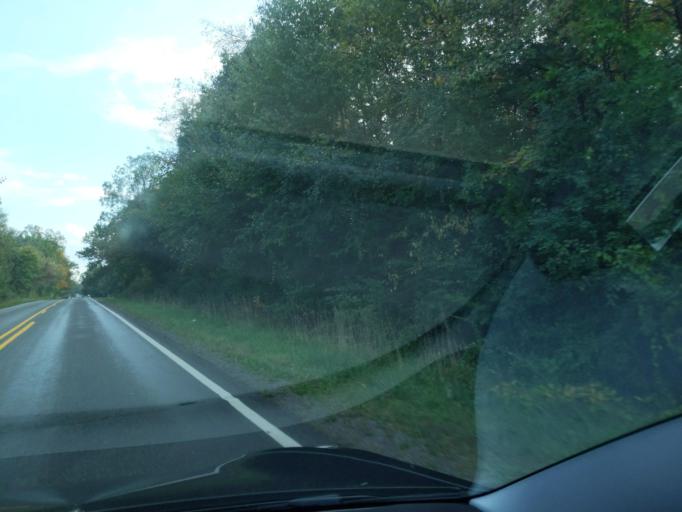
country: US
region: Michigan
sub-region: Jackson County
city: Jackson
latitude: 42.3025
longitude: -84.4627
